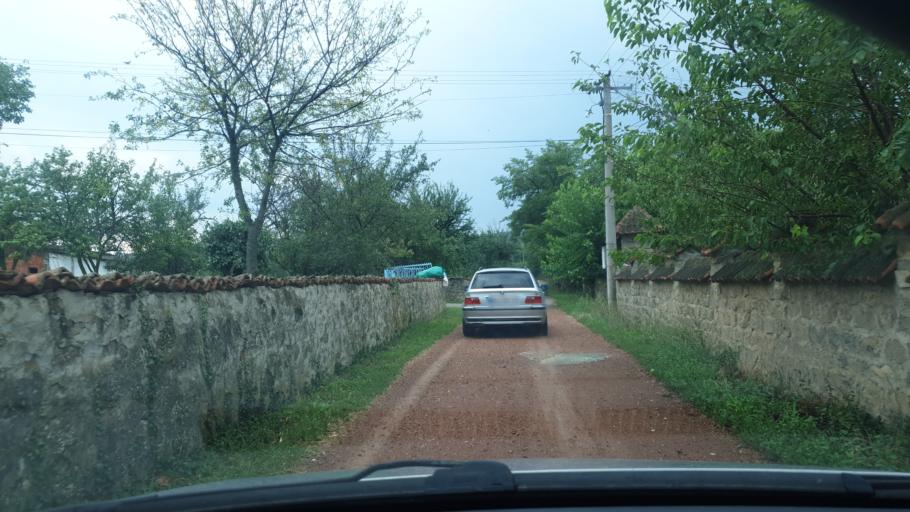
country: RS
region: Central Serbia
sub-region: Sumadijski Okrug
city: Kragujevac
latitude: 44.0781
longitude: 20.7978
